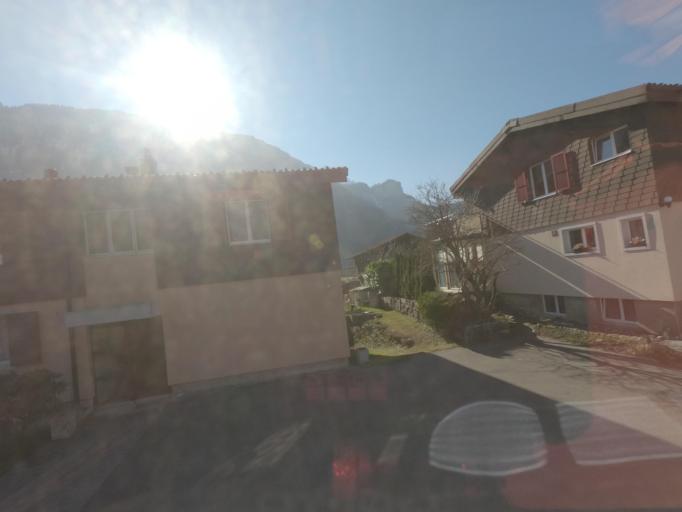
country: CH
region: Bern
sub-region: Interlaken-Oberhasli District
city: Meiringen
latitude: 46.7303
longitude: 8.1762
